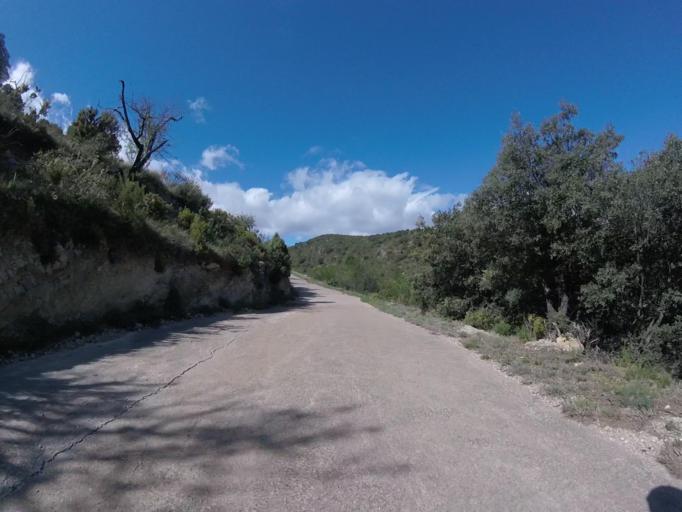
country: ES
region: Valencia
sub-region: Provincia de Castello
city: Culla
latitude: 40.3182
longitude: -0.0939
